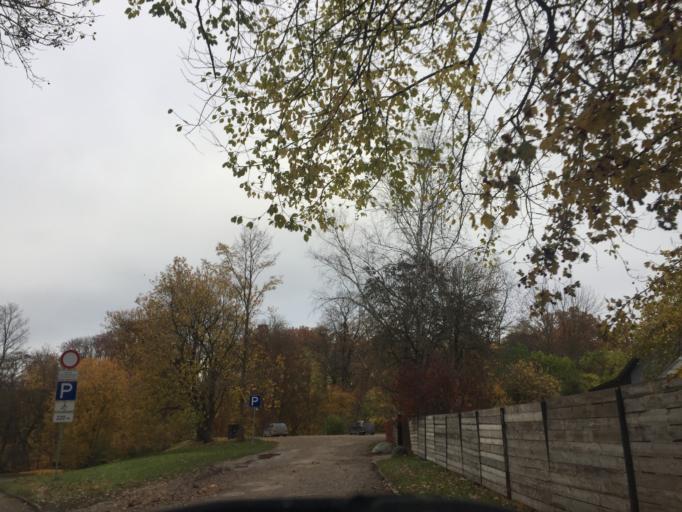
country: LV
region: Saldus Rajons
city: Saldus
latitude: 56.6669
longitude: 22.5103
